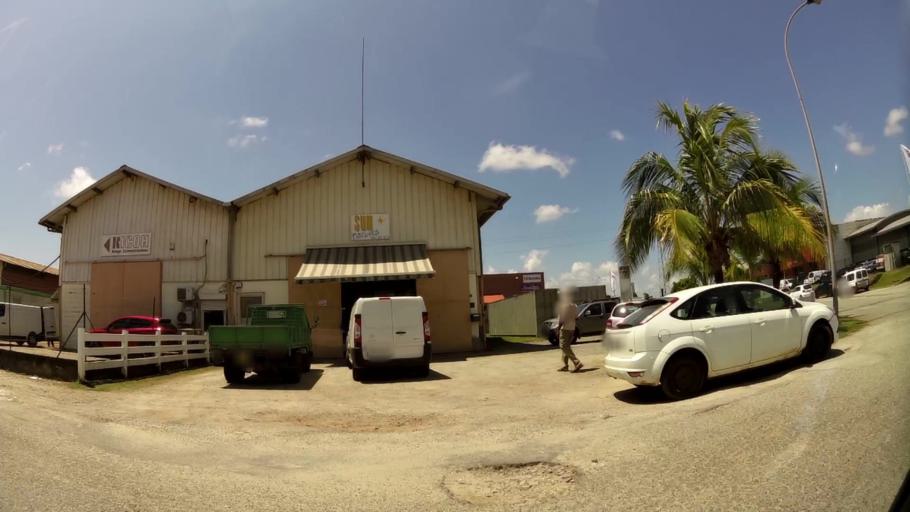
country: GF
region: Guyane
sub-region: Guyane
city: Cayenne
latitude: 4.8995
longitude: -52.3278
